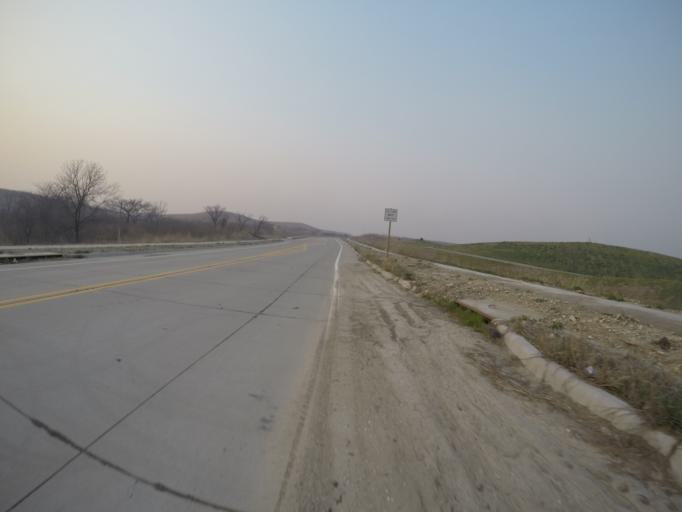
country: US
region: Kansas
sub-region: Riley County
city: Manhattan
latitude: 39.2177
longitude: -96.6445
